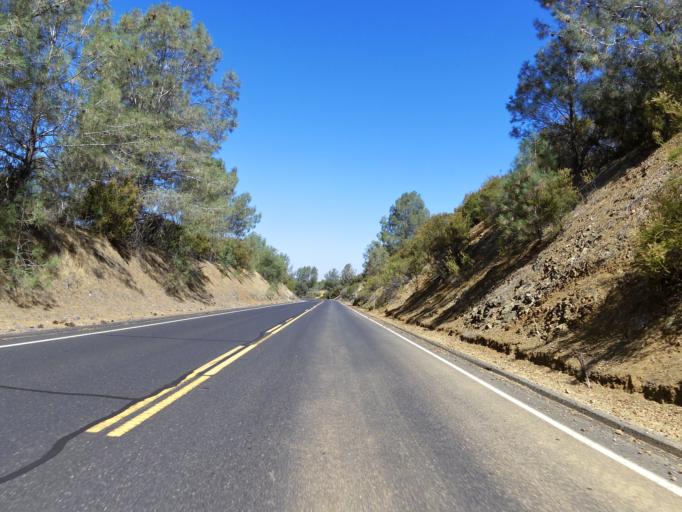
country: US
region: California
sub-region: Tuolumne County
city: Tuolumne City
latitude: 37.7127
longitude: -120.3175
